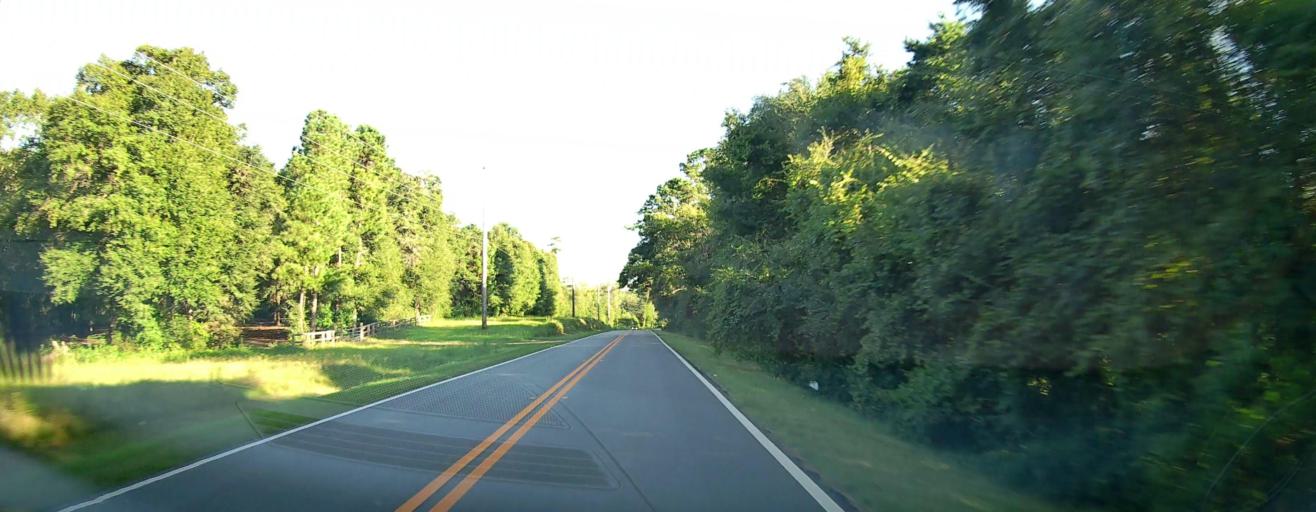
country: US
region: Georgia
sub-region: Pulaski County
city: Hawkinsville
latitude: 32.3058
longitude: -83.4508
